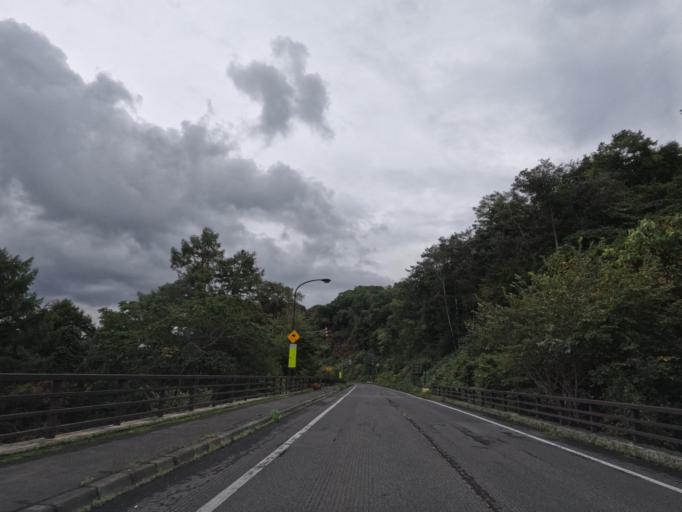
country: JP
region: Hokkaido
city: Date
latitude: 42.5326
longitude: 140.8606
